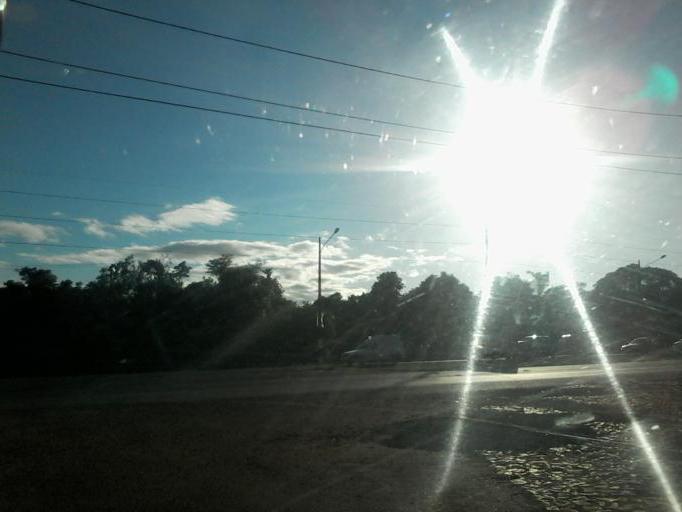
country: PY
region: Alto Parana
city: Ciudad del Este
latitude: -25.4345
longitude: -54.6377
